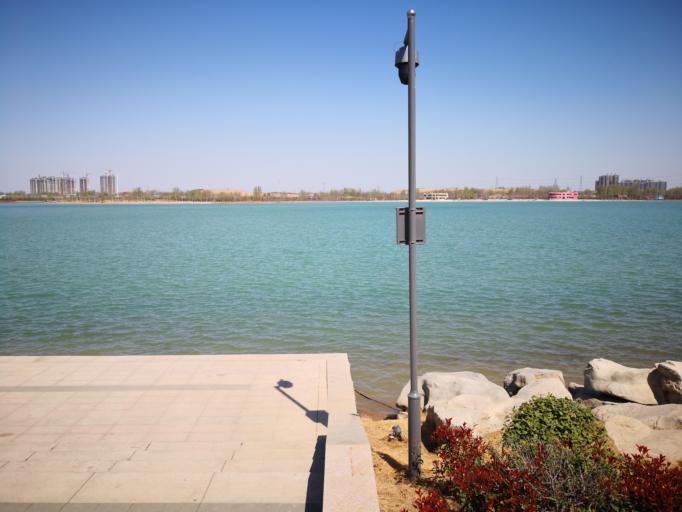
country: CN
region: Henan Sheng
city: Zhongyuanlu
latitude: 35.8003
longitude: 115.0546
